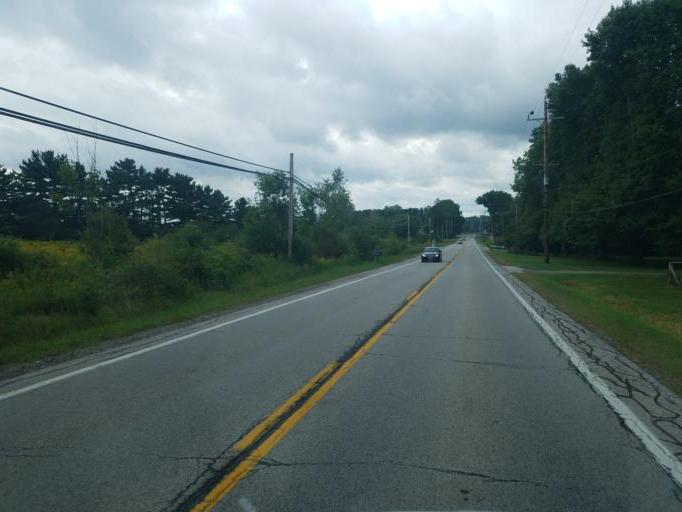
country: US
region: Ohio
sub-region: Geauga County
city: Chardon
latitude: 41.5875
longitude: -81.1829
